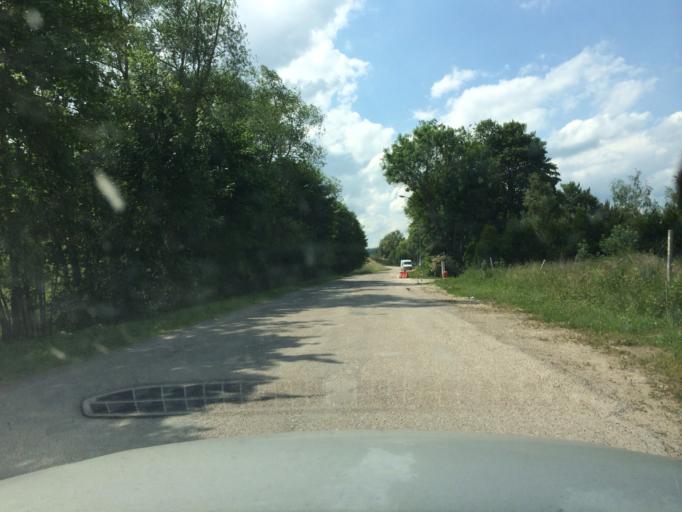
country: FR
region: Lorraine
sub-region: Departement de la Meuse
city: Vacon
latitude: 48.6869
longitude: 5.6302
